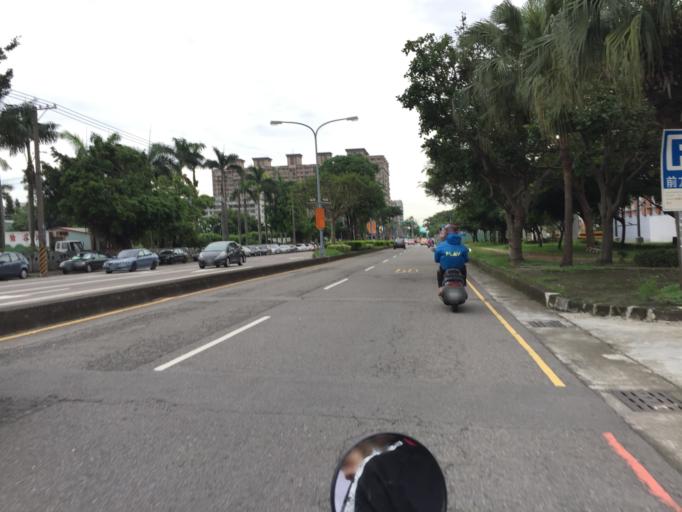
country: TW
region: Taiwan
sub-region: Taichung City
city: Taichung
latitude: 24.1574
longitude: 120.6991
